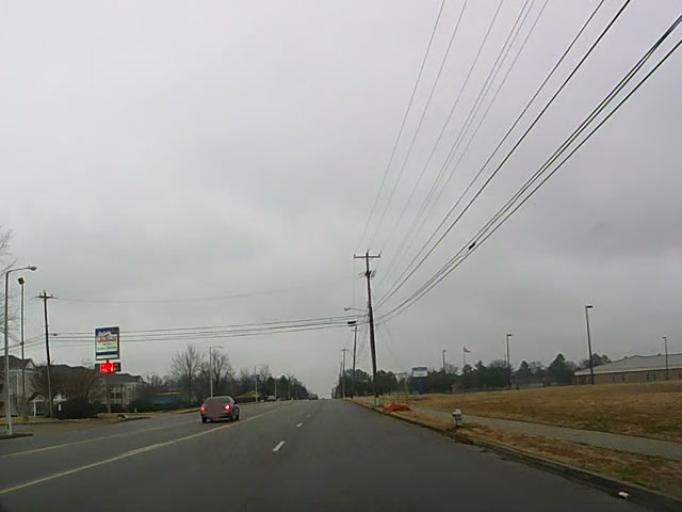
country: US
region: Tennessee
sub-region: Shelby County
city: Germantown
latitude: 35.0520
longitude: -89.8574
